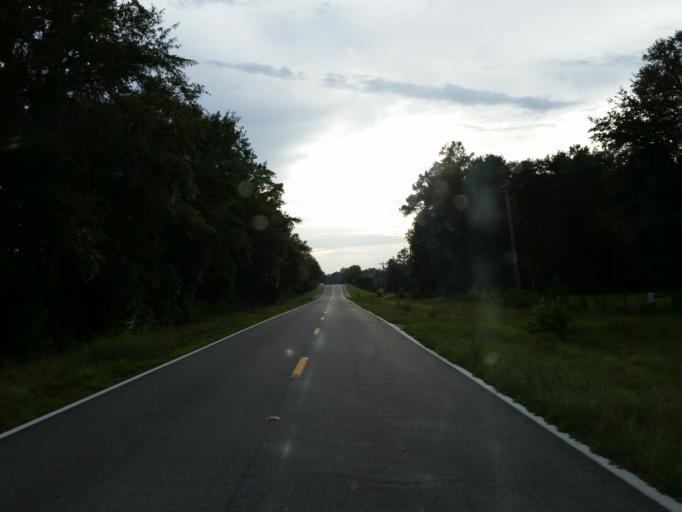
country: US
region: Florida
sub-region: Alachua County
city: High Springs
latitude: 29.9512
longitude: -82.5647
